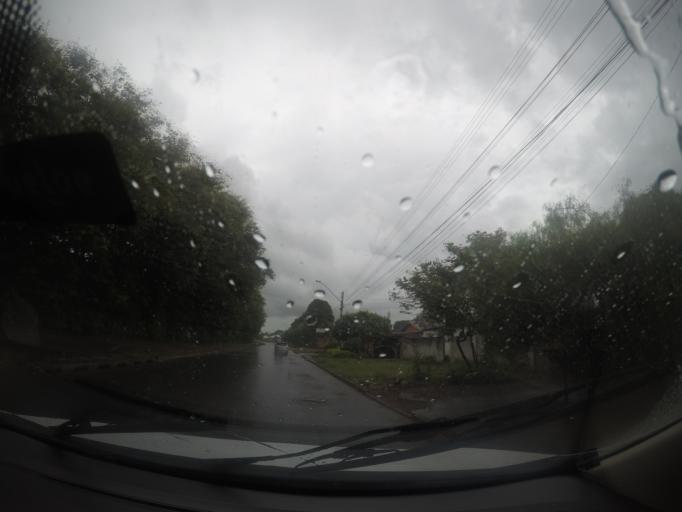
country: BR
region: Goias
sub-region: Trindade
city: Trindade
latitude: -16.6462
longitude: -49.3908
